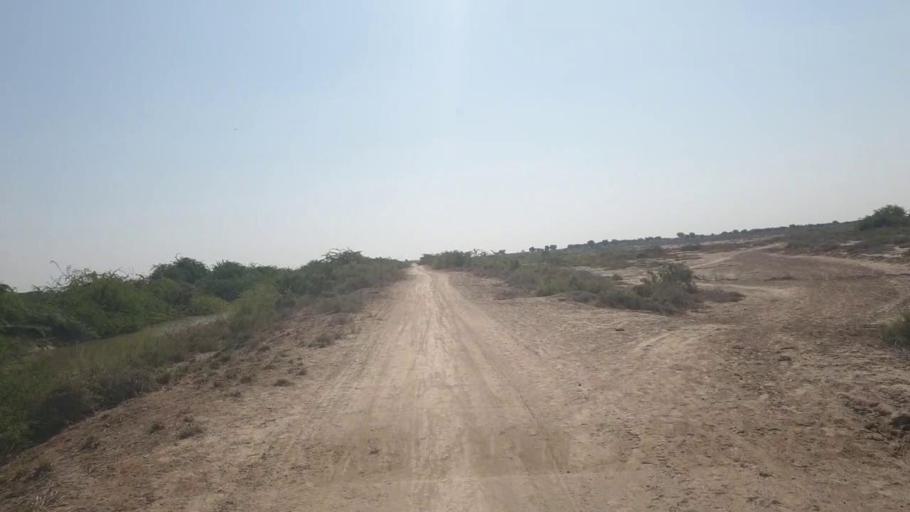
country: PK
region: Sindh
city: Tando Bago
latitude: 24.8848
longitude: 69.1645
